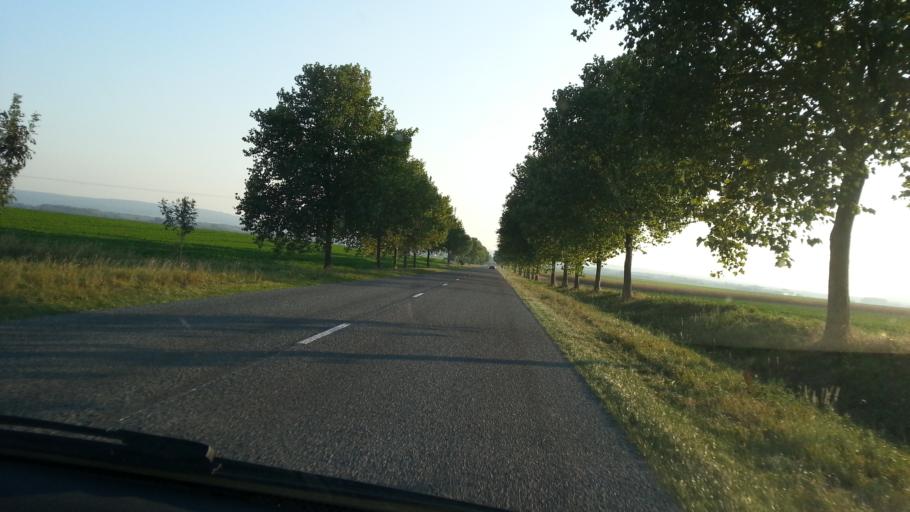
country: FR
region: Picardie
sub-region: Departement de l'Oise
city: Saint-Martin-Longueau
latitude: 49.3680
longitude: 2.6148
